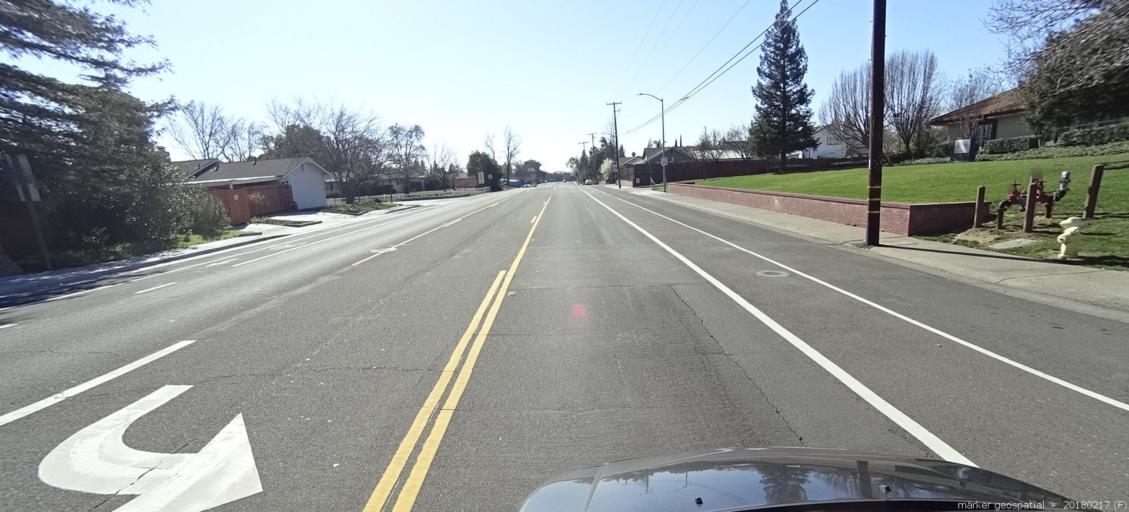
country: US
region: California
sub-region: Sacramento County
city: Orangevale
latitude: 38.6657
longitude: -121.2026
